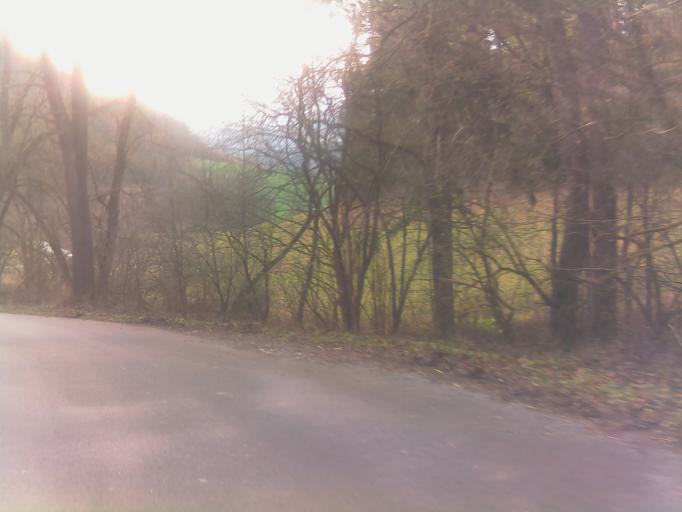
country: DE
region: Thuringia
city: Rottenbach
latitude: 50.7261
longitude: 11.1986
